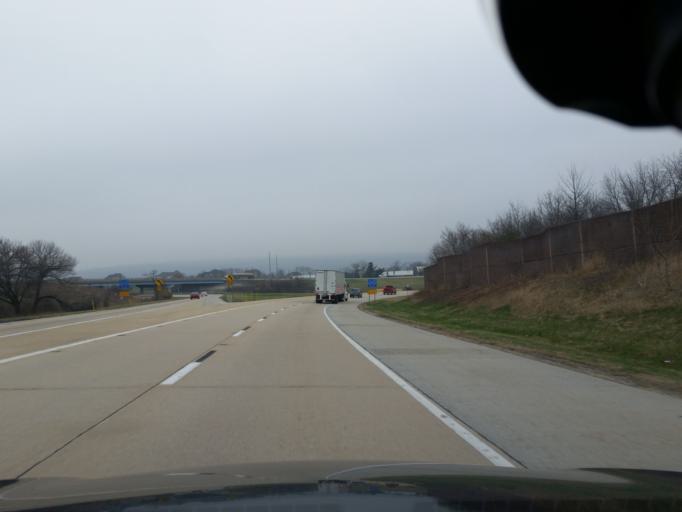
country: US
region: Pennsylvania
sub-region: Cumberland County
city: Mechanicsburg
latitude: 40.2714
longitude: -77.0001
